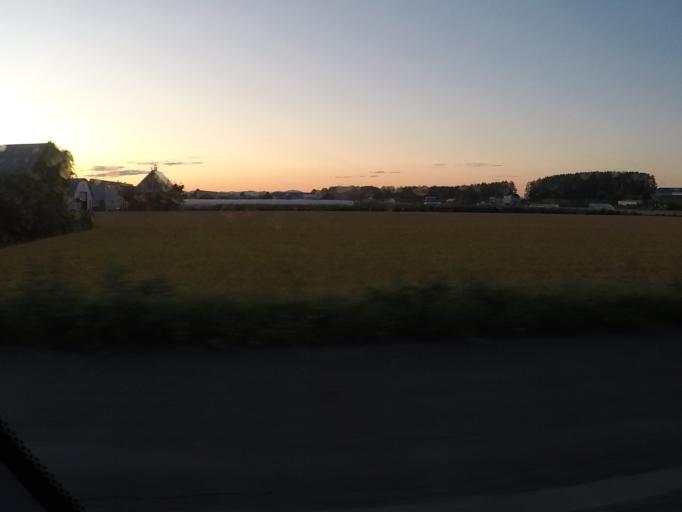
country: JP
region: Hokkaido
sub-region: Asahikawa-shi
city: Asahikawa
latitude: 43.6785
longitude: 142.4581
